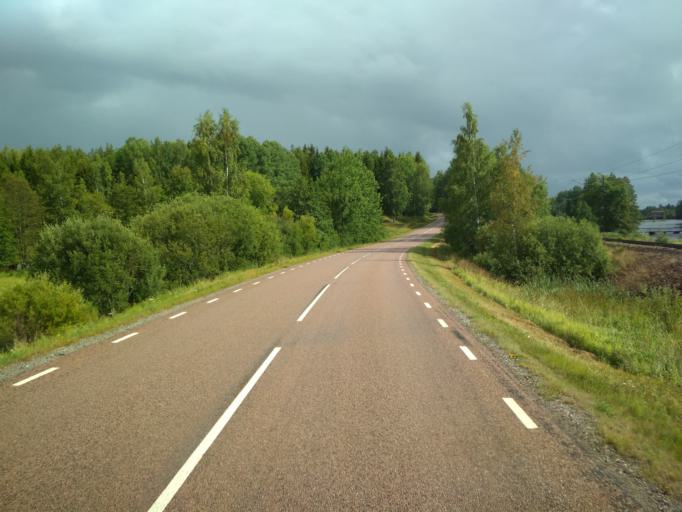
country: SE
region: Vaestmanland
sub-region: Surahammars Kommun
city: Ramnas
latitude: 59.8299
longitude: 16.1395
